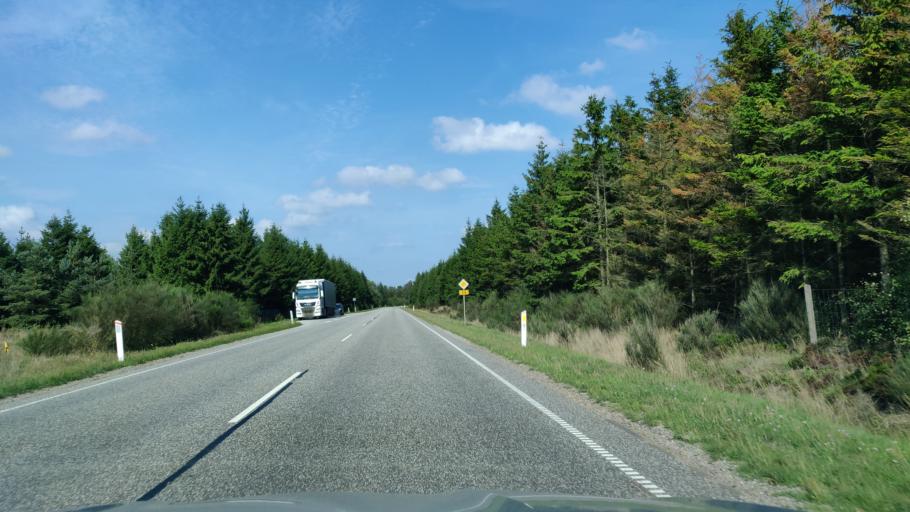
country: DK
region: Central Jutland
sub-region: Herning Kommune
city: Sunds
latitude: 56.3492
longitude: 8.9748
